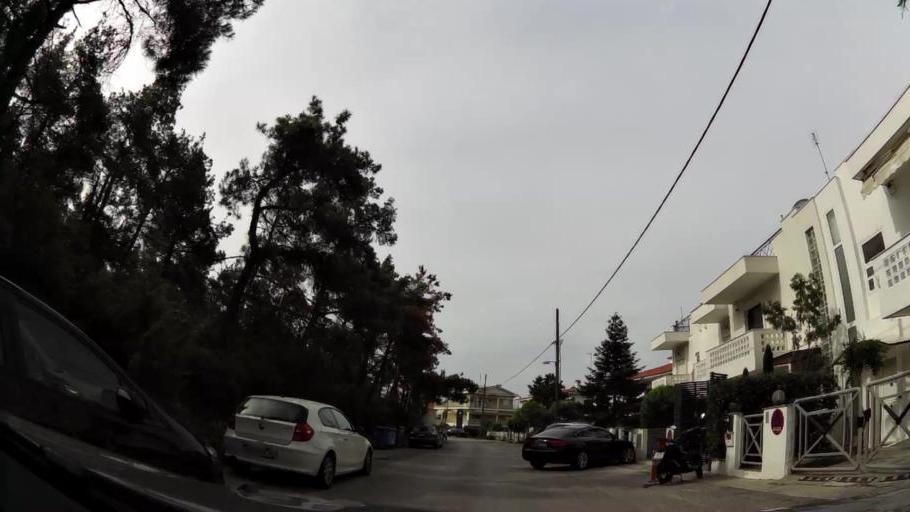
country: GR
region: Central Macedonia
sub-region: Nomos Thessalonikis
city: Panorama
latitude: 40.5878
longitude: 23.0300
